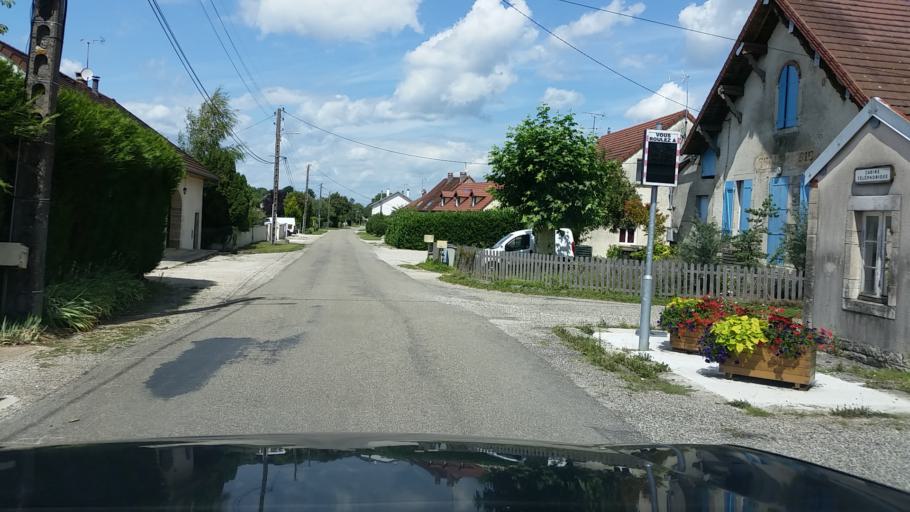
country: FR
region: Franche-Comte
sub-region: Departement du Jura
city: Bletterans
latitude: 46.7856
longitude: 5.5078
